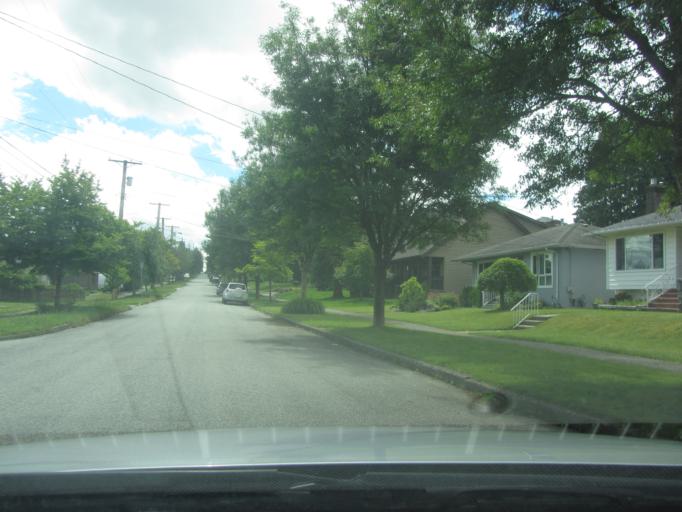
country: CA
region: British Columbia
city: New Westminster
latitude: 49.2198
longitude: -122.9244
